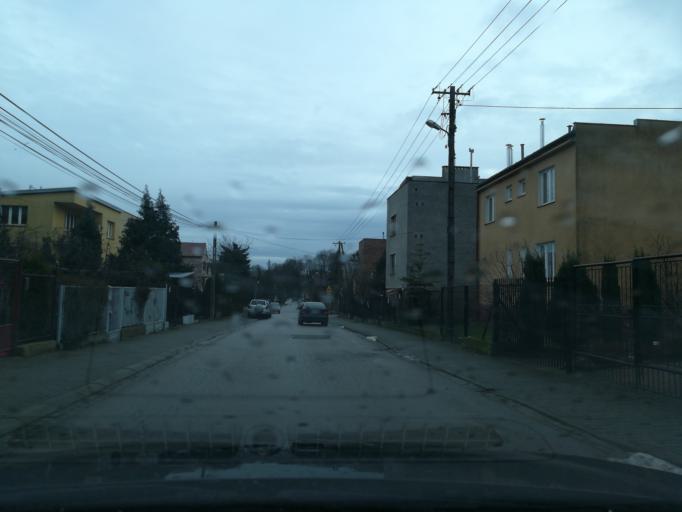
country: PL
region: Lesser Poland Voivodeship
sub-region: Krakow
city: Krakow
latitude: 50.0215
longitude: 19.9920
